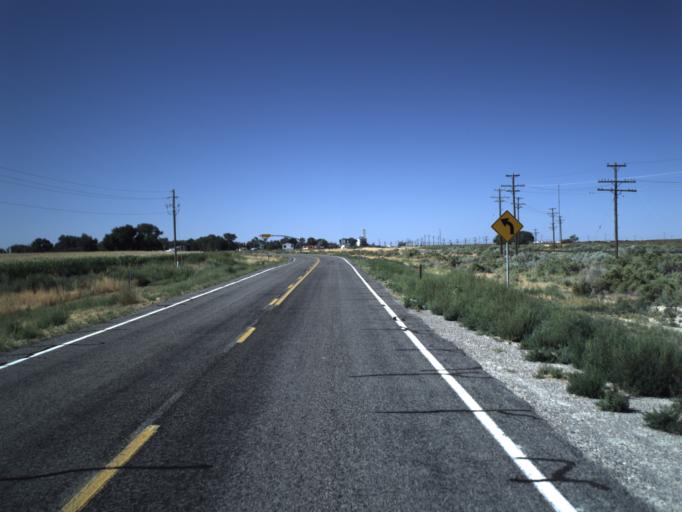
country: US
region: Utah
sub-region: Millard County
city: Delta
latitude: 39.5293
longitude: -112.3704
